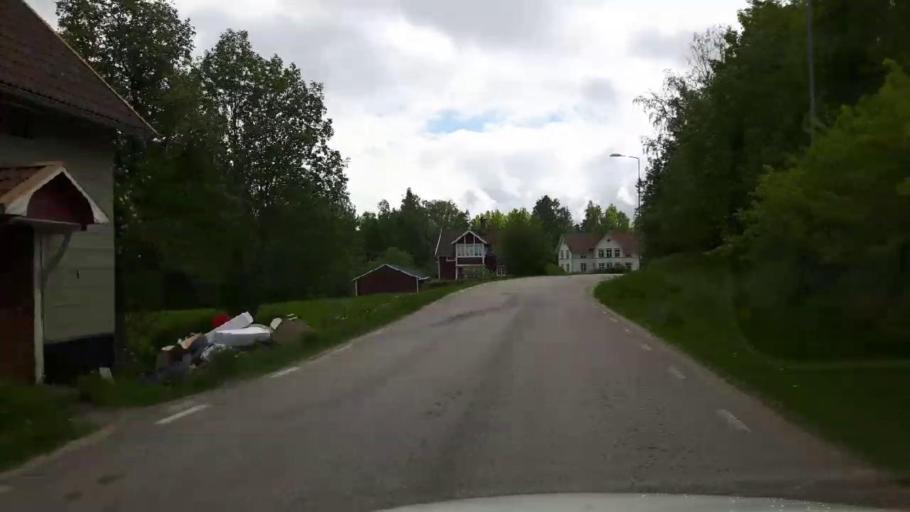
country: SE
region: Gaevleborg
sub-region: Ovanakers Kommun
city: Alfta
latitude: 61.3377
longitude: 15.9563
